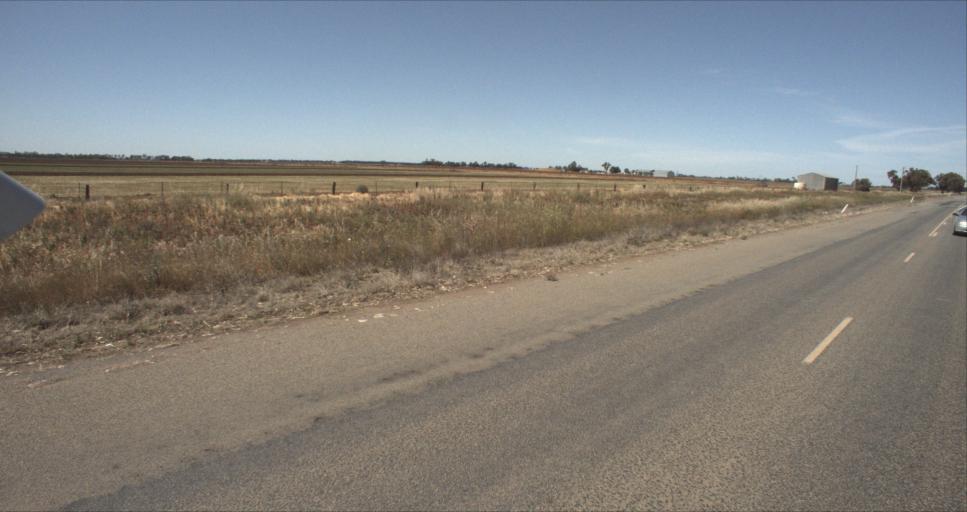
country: AU
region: New South Wales
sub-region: Leeton
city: Leeton
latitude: -34.4983
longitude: 146.2874
